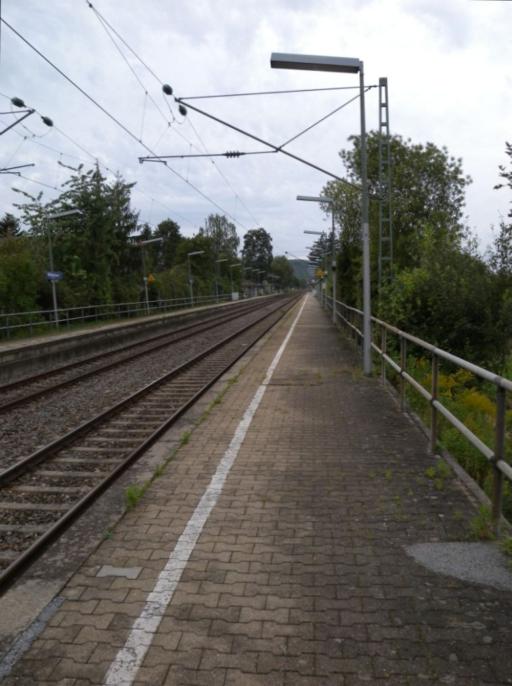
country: DE
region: Baden-Wuerttemberg
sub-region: Regierungsbezirk Stuttgart
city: Schorndorf
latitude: 48.8005
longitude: 9.5037
